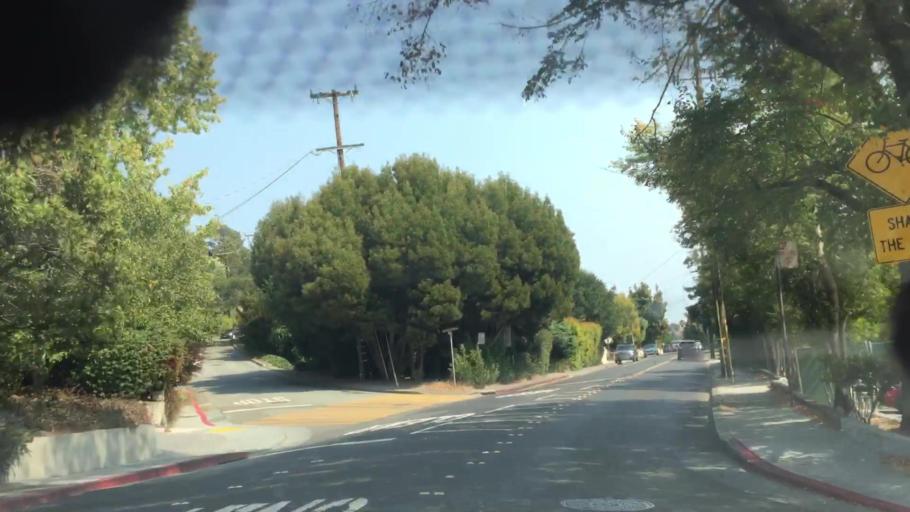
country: US
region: California
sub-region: Marin County
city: Mill Valley
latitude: 37.9037
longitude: -122.5366
